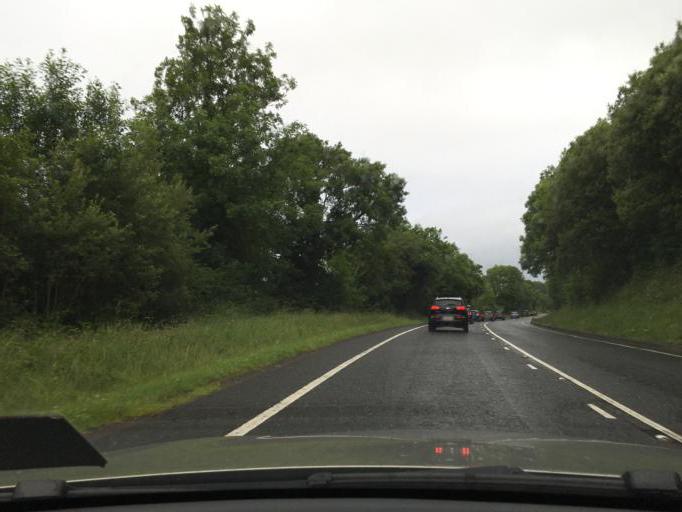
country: GB
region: Northern Ireland
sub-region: Fermanagh District
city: Enniskillen
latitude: 54.3793
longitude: -7.6367
